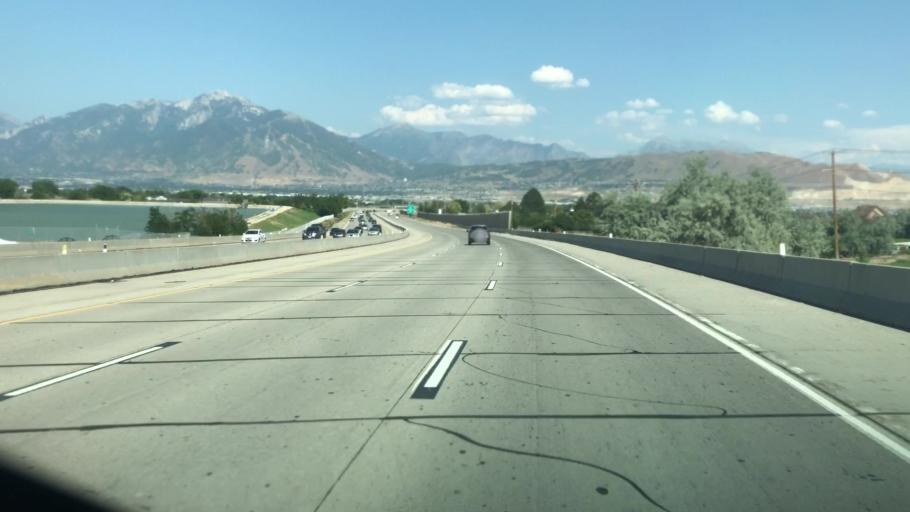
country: US
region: Utah
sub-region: Salt Lake County
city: Bluffdale
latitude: 40.5007
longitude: -111.9735
